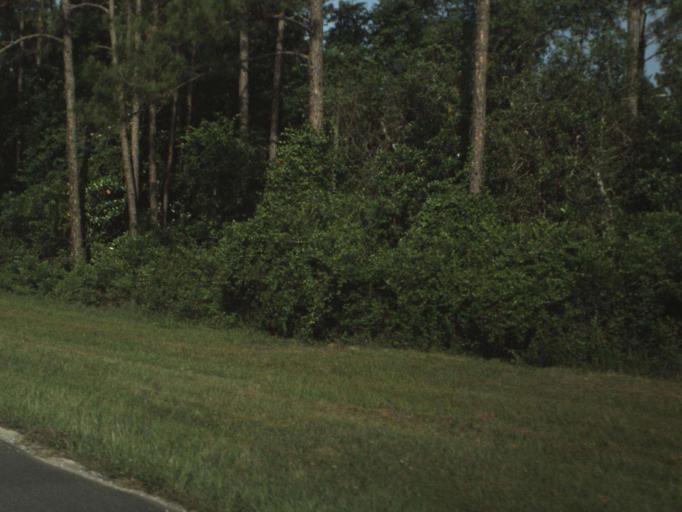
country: US
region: Florida
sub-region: Volusia County
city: North DeLand
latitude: 29.0730
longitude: -81.2506
